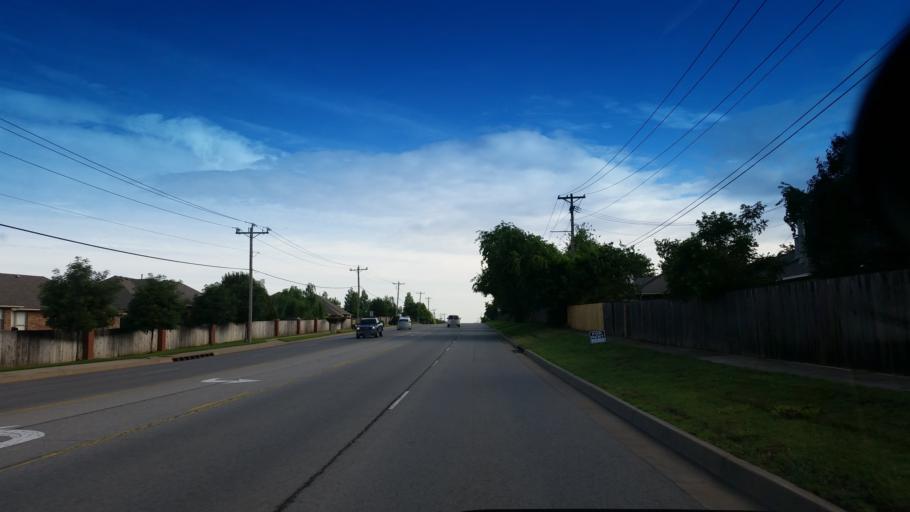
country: US
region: Oklahoma
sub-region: Oklahoma County
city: Edmond
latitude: 35.6303
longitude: -97.5137
